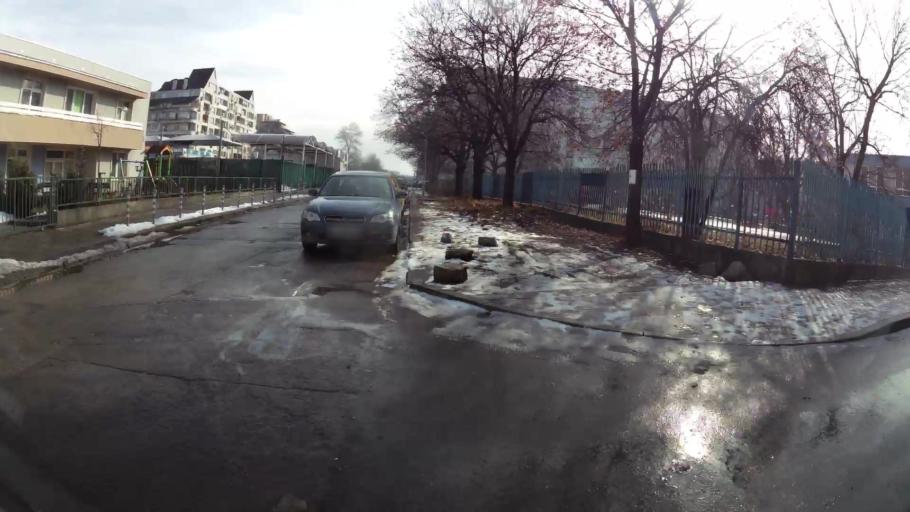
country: BG
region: Sofia-Capital
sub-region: Stolichna Obshtina
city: Sofia
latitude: 42.7224
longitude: 23.2650
